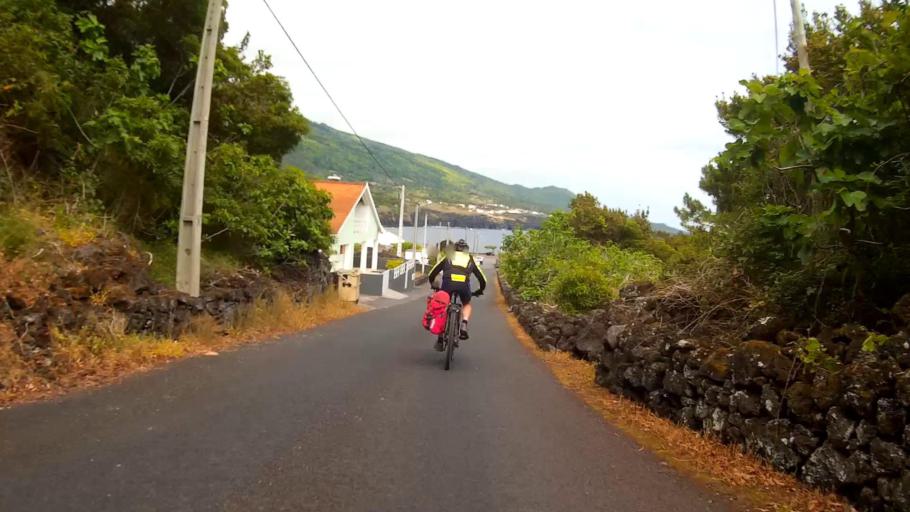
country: PT
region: Azores
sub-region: Sao Roque do Pico
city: Sao Roque do Pico
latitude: 38.4262
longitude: -28.4244
